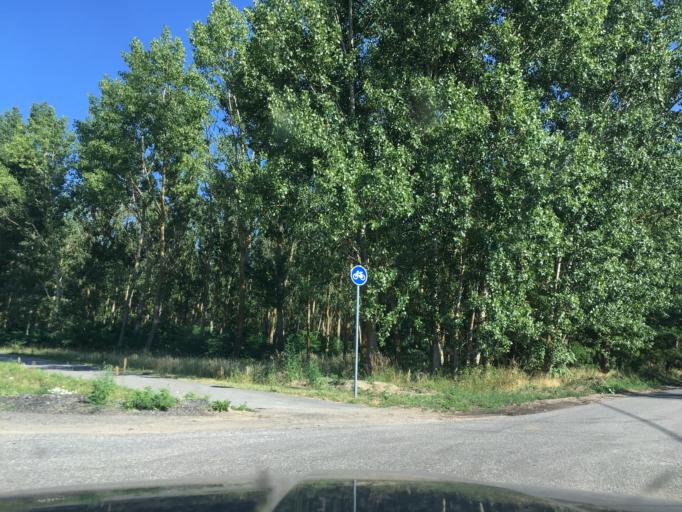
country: HU
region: Hajdu-Bihar
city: Hajdusamson
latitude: 47.6438
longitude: 21.8252
